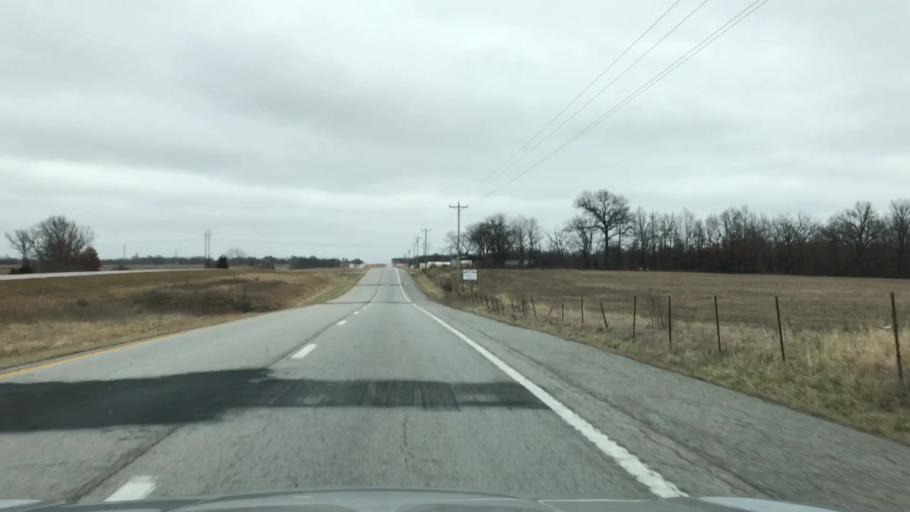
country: US
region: Missouri
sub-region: Linn County
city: Linneus
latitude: 39.7780
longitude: -93.2004
